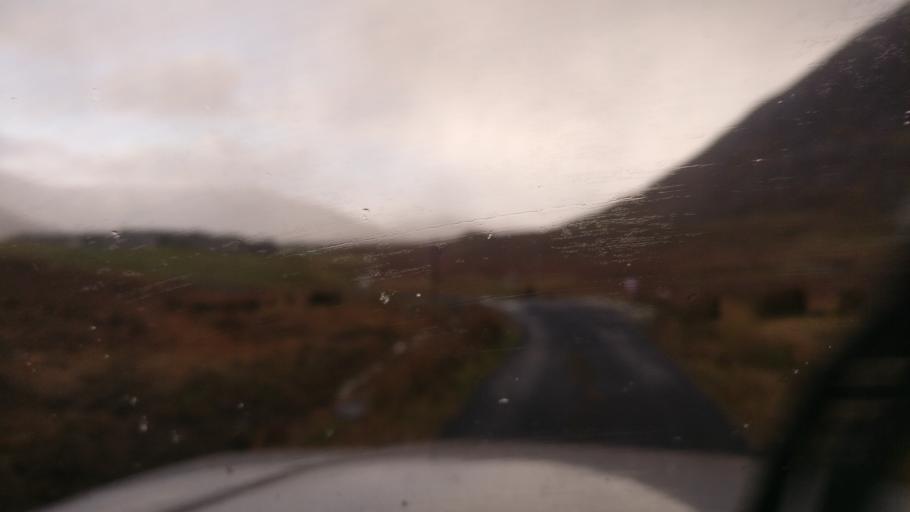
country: IE
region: Connaught
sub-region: County Galway
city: Clifden
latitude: 53.5180
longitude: -9.7201
